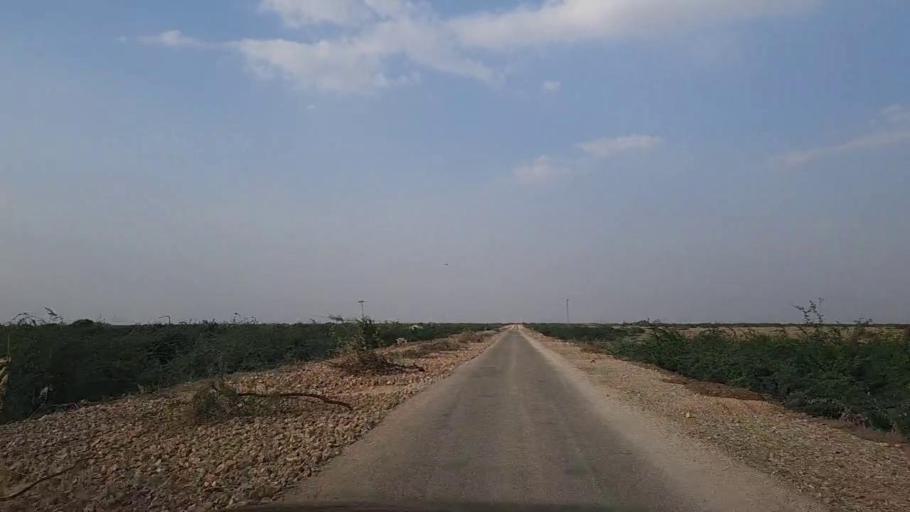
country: PK
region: Sindh
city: Gharo
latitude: 24.8398
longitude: 67.7458
